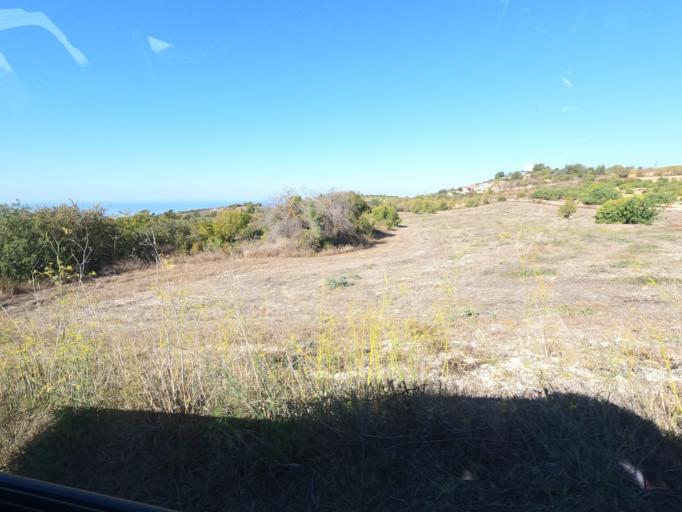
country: CY
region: Pafos
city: Mesogi
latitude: 34.8030
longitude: 32.4935
